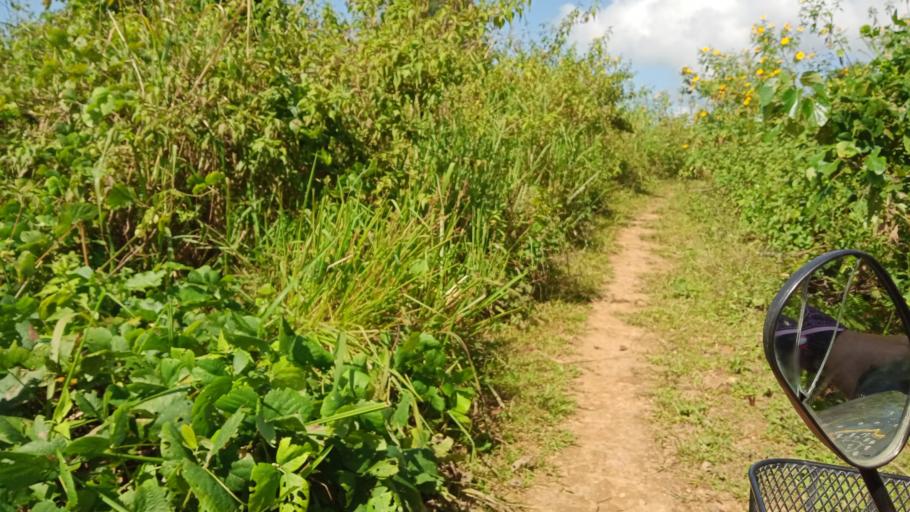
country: LA
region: Xiangkhoang
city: Phonsavan
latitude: 19.1167
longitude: 102.9199
